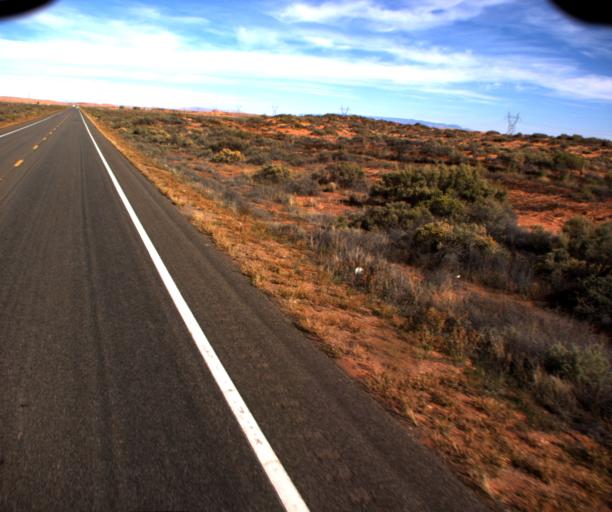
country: US
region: Arizona
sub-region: Navajo County
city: Kayenta
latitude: 36.8050
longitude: -109.9141
